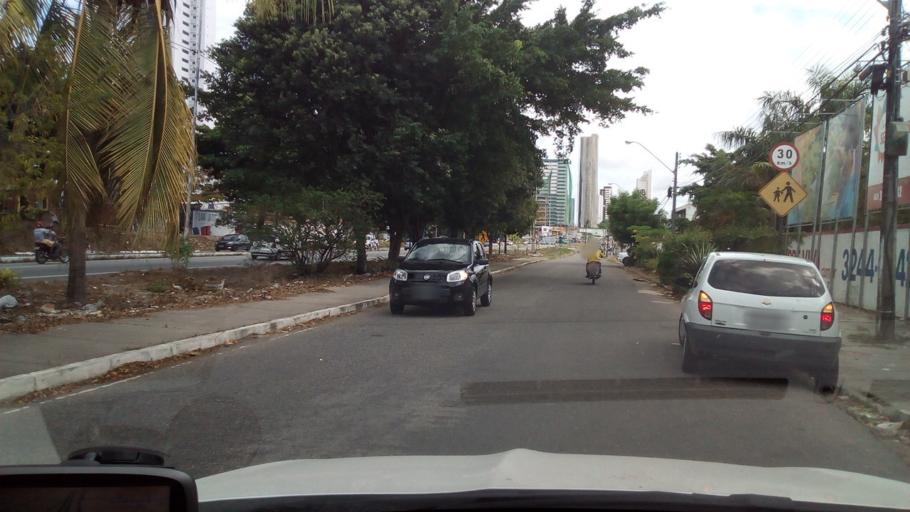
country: BR
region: Paraiba
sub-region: Joao Pessoa
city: Joao Pessoa
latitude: -7.1107
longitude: -34.8431
